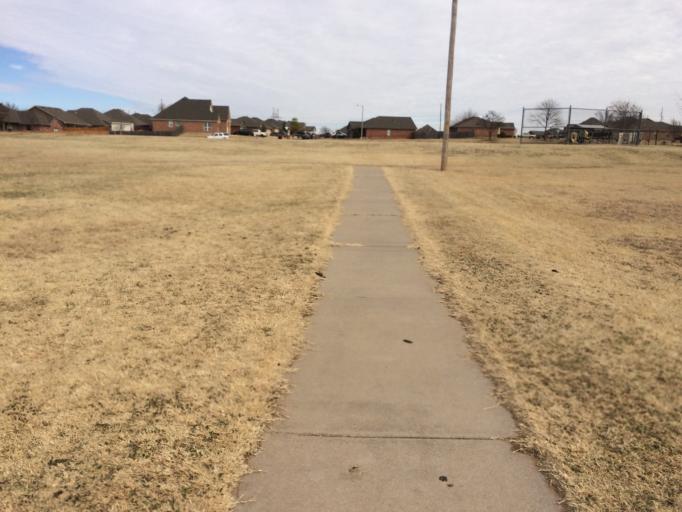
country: US
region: Oklahoma
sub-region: Cleveland County
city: Hall Park
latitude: 35.2242
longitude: -97.4008
